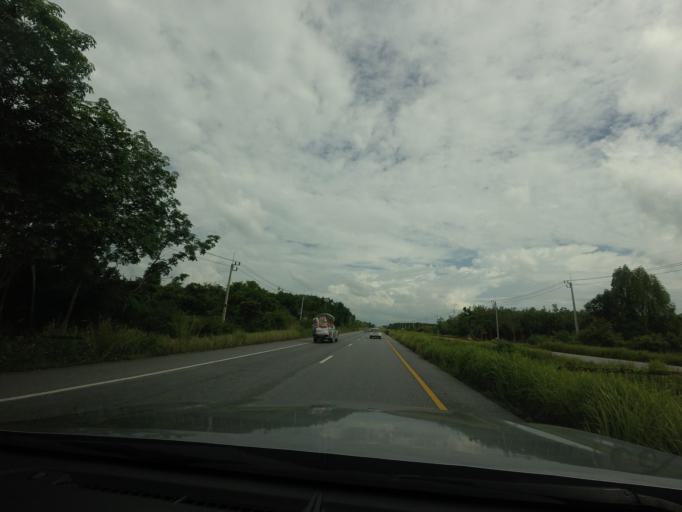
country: TH
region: Pattani
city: Mae Lan
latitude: 6.7096
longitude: 101.2285
